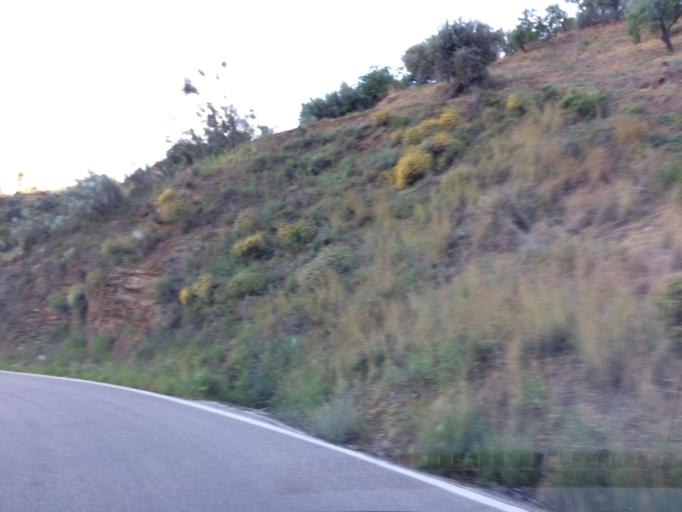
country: ES
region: Andalusia
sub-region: Provincia de Malaga
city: Totalan
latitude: 36.7774
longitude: -4.3214
